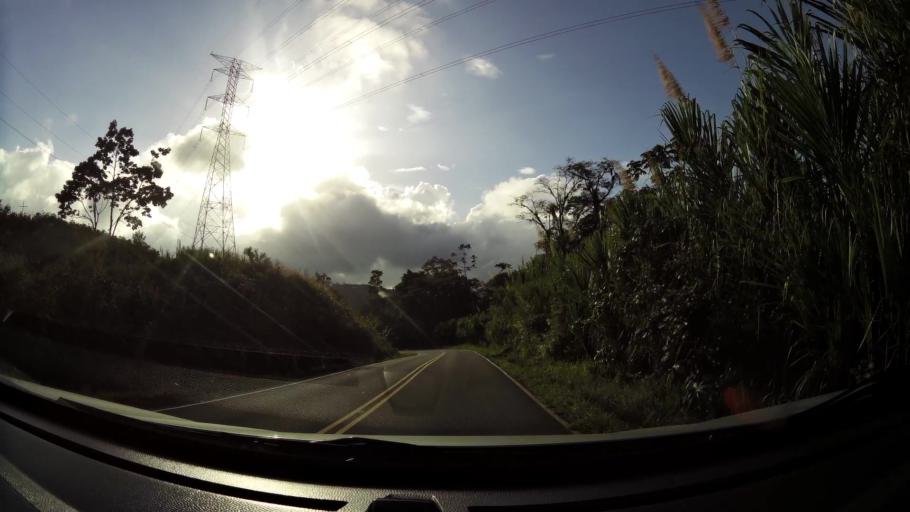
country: CR
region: Limon
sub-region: Canton de Siquirres
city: Siquirres
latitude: 10.0321
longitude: -83.5520
